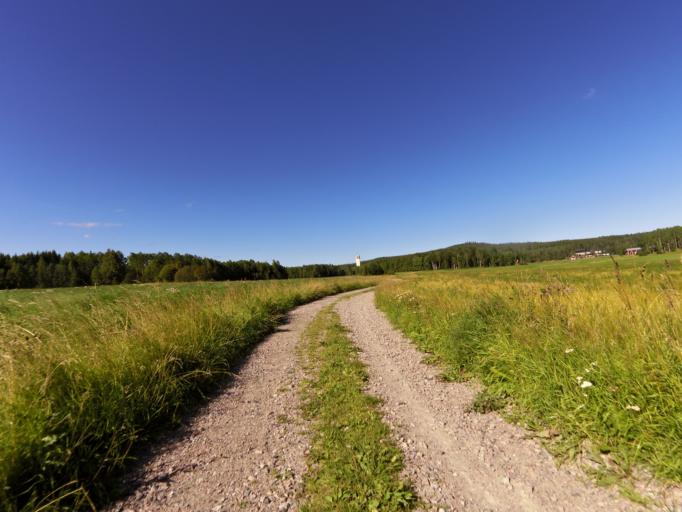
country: SE
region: Gaevleborg
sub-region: Hofors Kommun
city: Hofors
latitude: 60.5227
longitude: 16.4093
